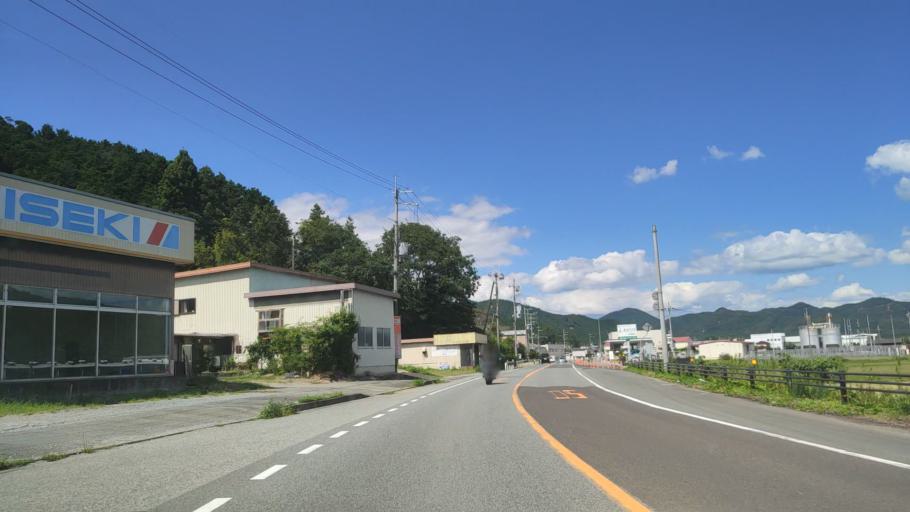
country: JP
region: Kyoto
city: Fukuchiyama
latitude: 35.2173
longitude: 135.1320
